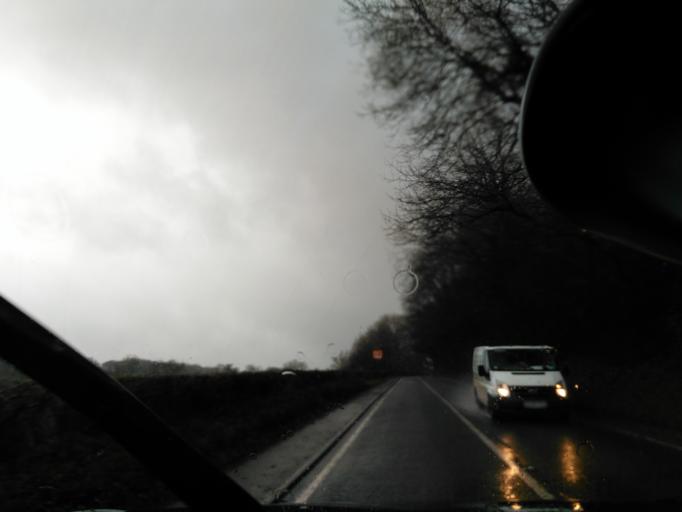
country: GB
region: England
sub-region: Somerset
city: Shepton Mallet
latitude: 51.1854
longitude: -2.5152
